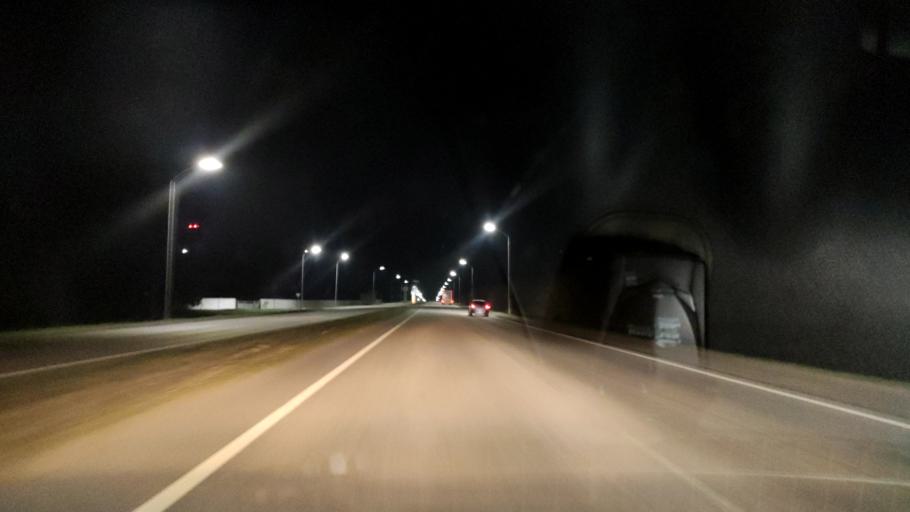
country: RU
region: Belgorod
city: Staryy Oskol
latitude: 51.3662
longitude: 37.8417
